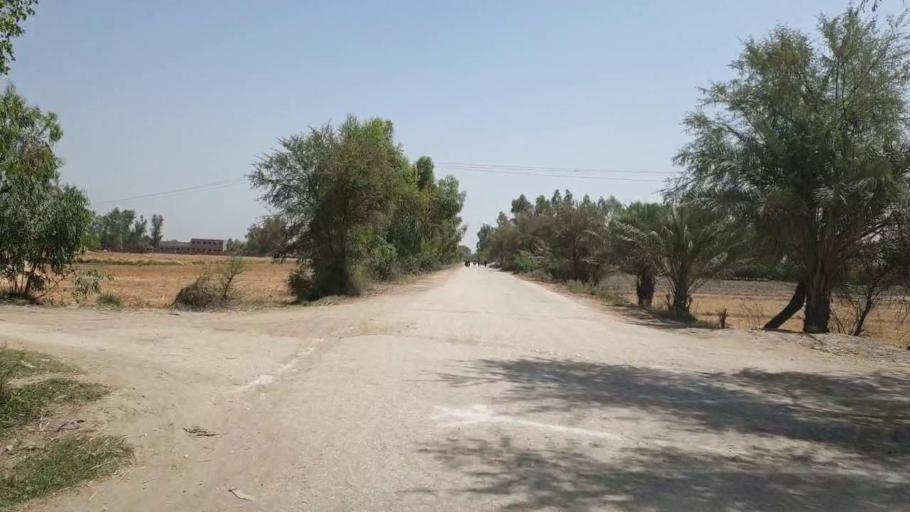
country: PK
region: Sindh
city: Adilpur
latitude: 27.8415
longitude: 69.2672
